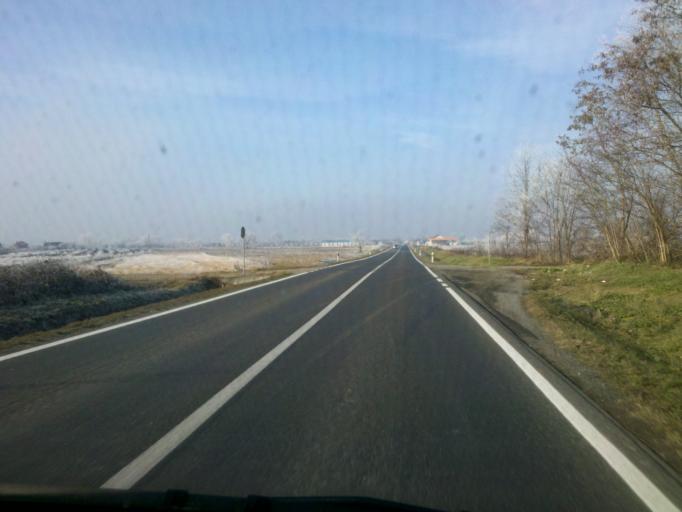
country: HR
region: Virovitick-Podravska
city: Pitomaca
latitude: 45.9723
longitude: 17.1759
